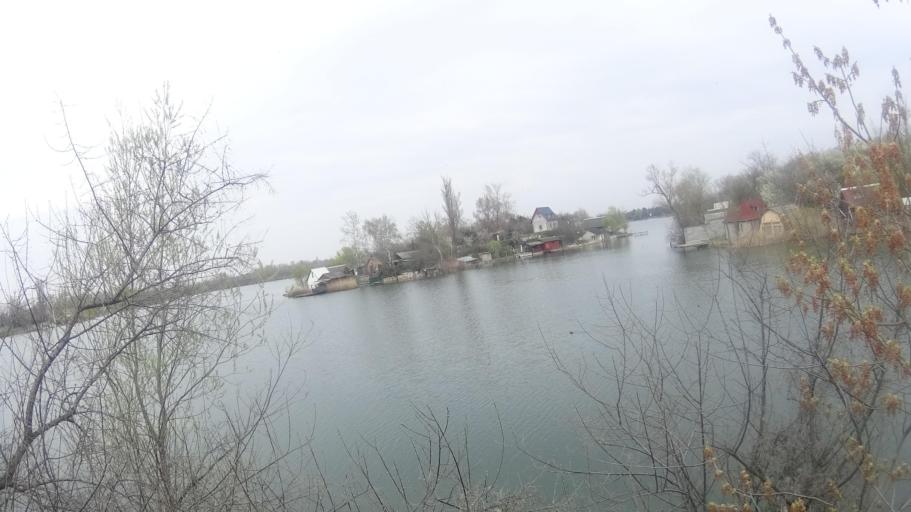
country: HU
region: Pest
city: Szigetszentmiklos
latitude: 47.3853
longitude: 19.0539
